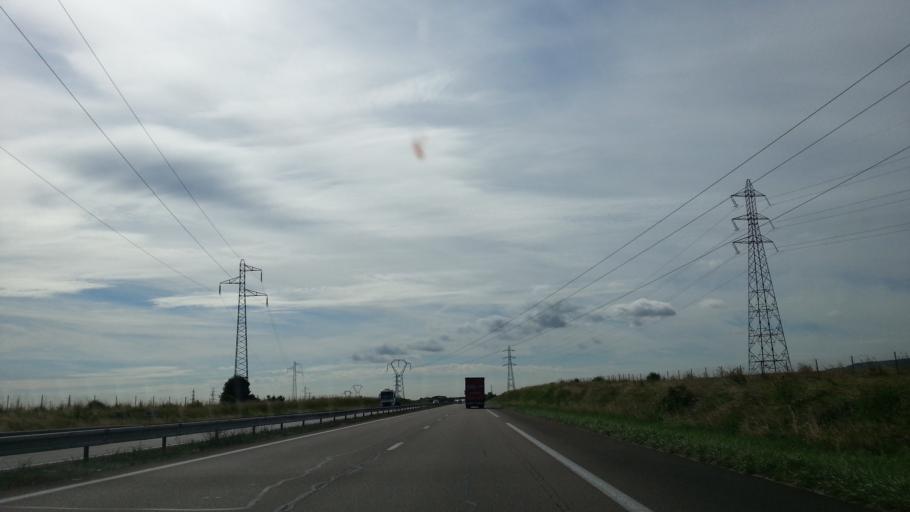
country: FR
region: Champagne-Ardenne
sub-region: Departement de la Marne
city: Sillery
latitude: 49.1832
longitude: 4.1508
